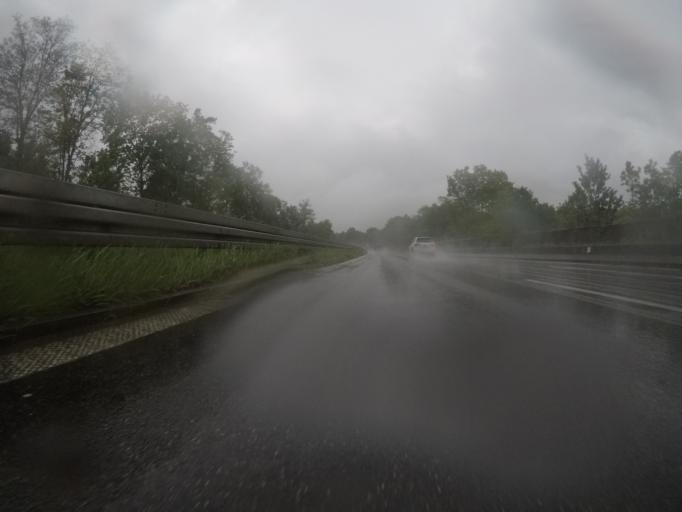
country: DE
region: Baden-Wuerttemberg
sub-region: Regierungsbezirk Stuttgart
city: Leinfelden-Echterdingen
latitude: 48.7289
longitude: 9.1666
